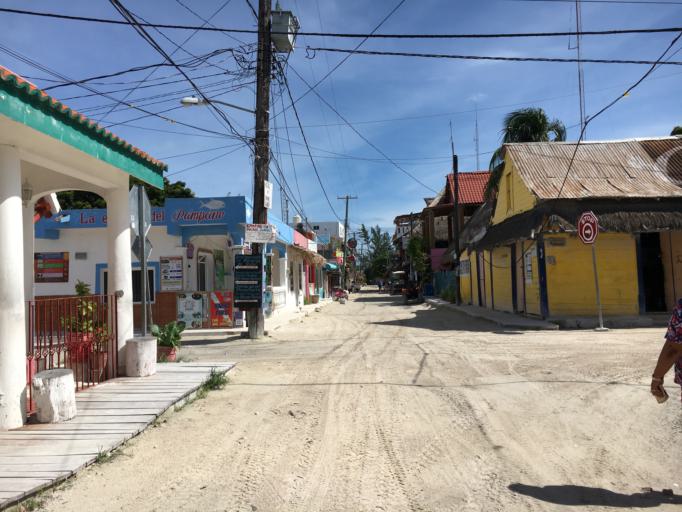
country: MX
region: Quintana Roo
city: Kantunilkin
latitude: 21.5242
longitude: -87.3790
